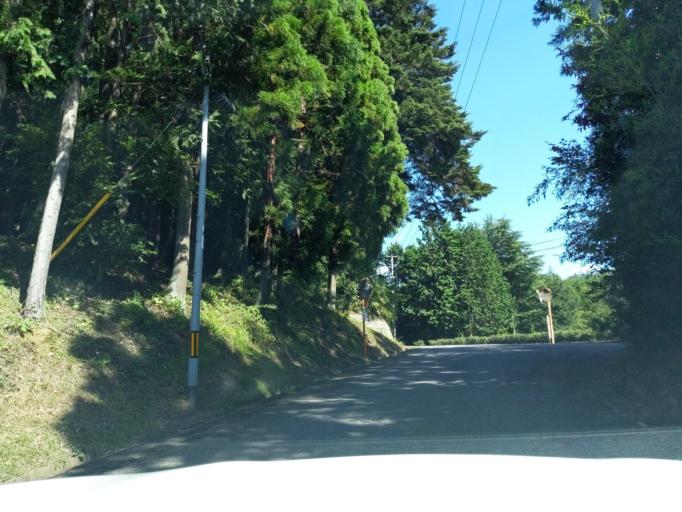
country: JP
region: Fukushima
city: Koriyama
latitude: 37.3754
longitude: 140.2884
